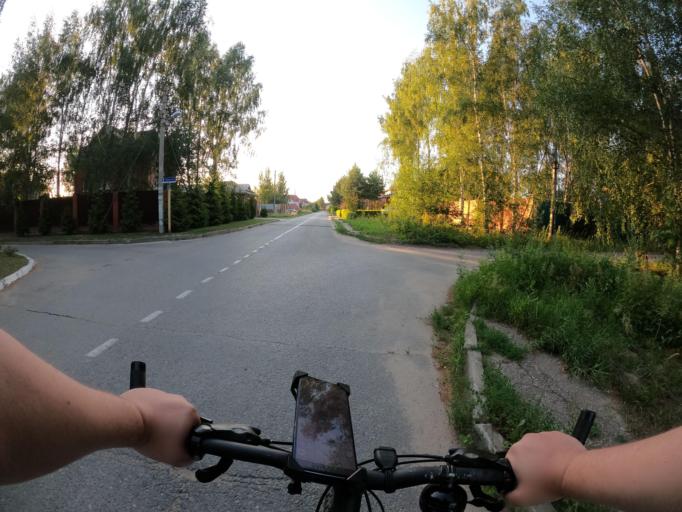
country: RU
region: Moskovskaya
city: Beloozerskiy
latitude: 55.4660
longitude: 38.4289
